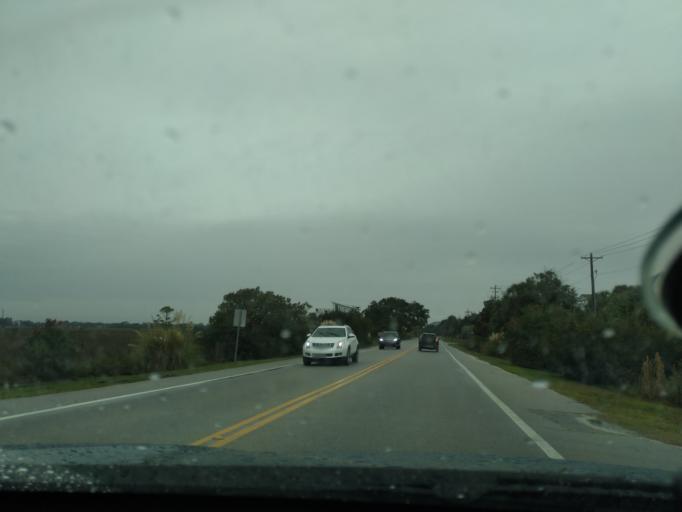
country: US
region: South Carolina
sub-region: Charleston County
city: Folly Beach
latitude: 32.6699
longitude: -79.9474
